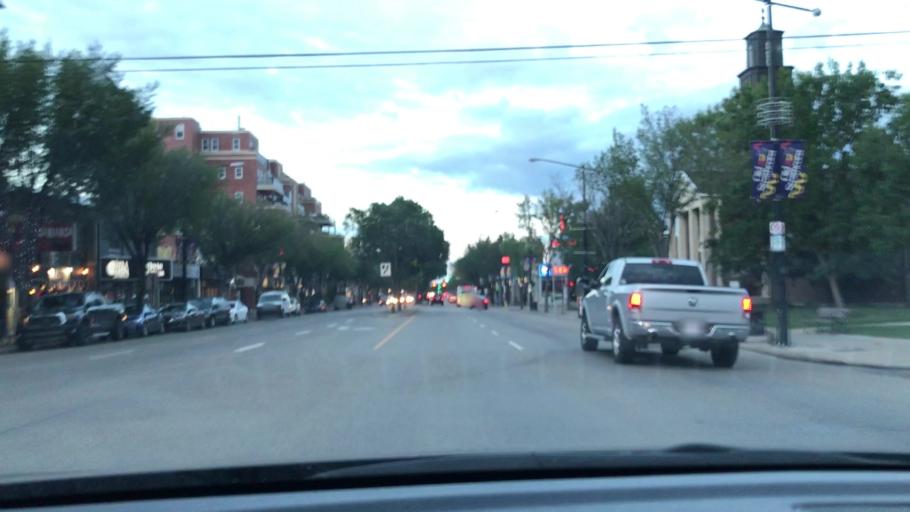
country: CA
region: Alberta
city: Edmonton
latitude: 53.5181
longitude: -113.5095
